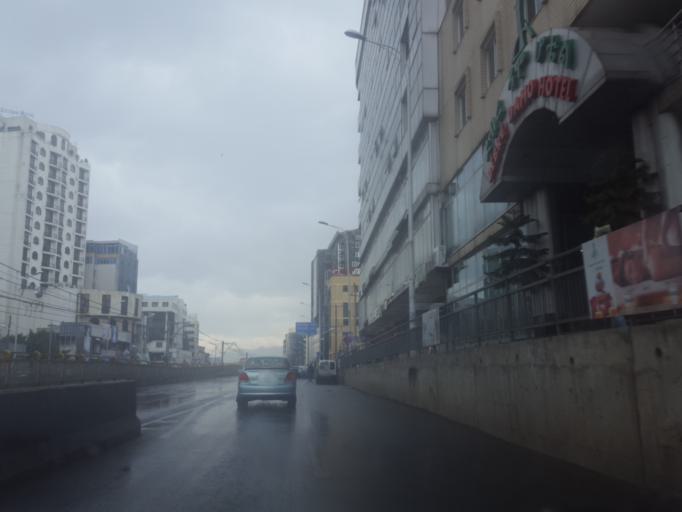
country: ET
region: Adis Abeba
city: Addis Ababa
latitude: 9.0154
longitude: 38.7852
